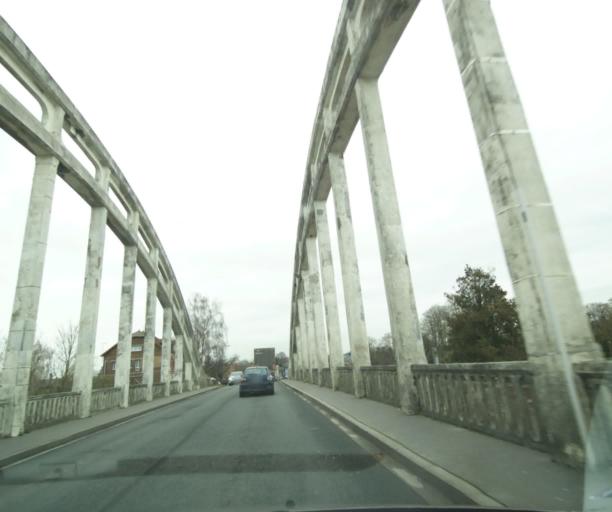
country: FR
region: Picardie
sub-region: Departement de l'Oise
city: Noyon
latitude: 49.5767
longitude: 3.0055
